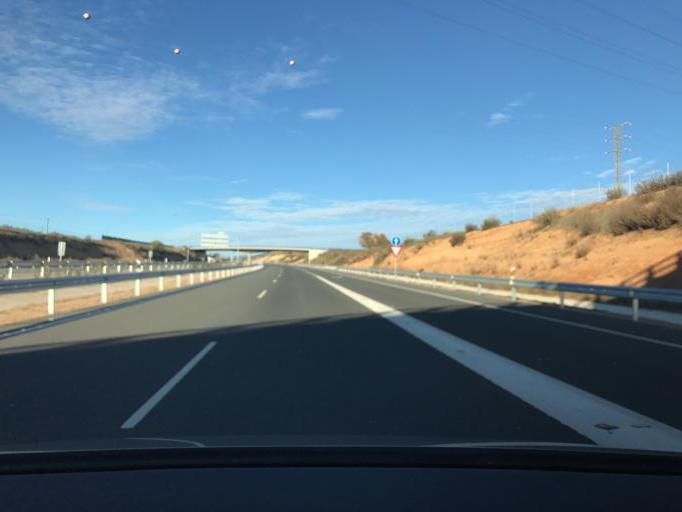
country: ES
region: Andalusia
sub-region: Provincia de Granada
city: Albolote
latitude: 37.2355
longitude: -3.6638
